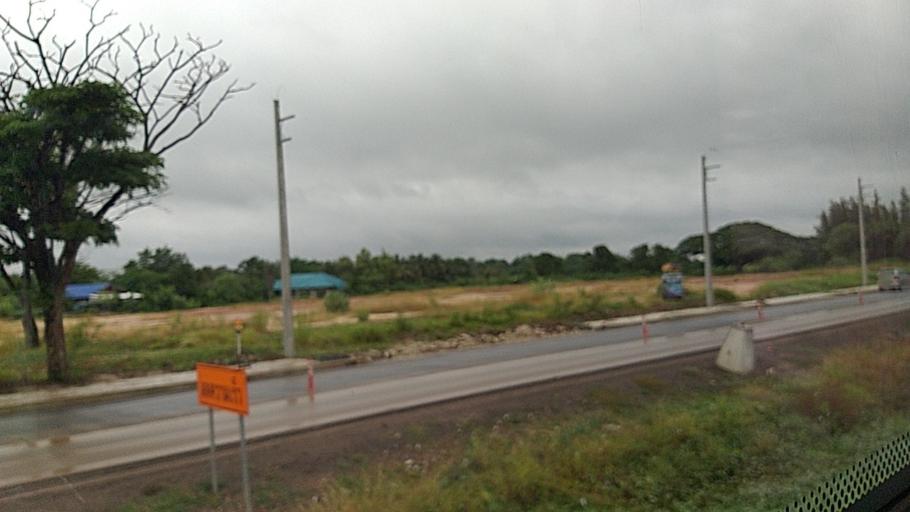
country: TH
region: Nakhon Ratchasima
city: Nakhon Ratchasima
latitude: 14.9915
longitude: 102.0622
